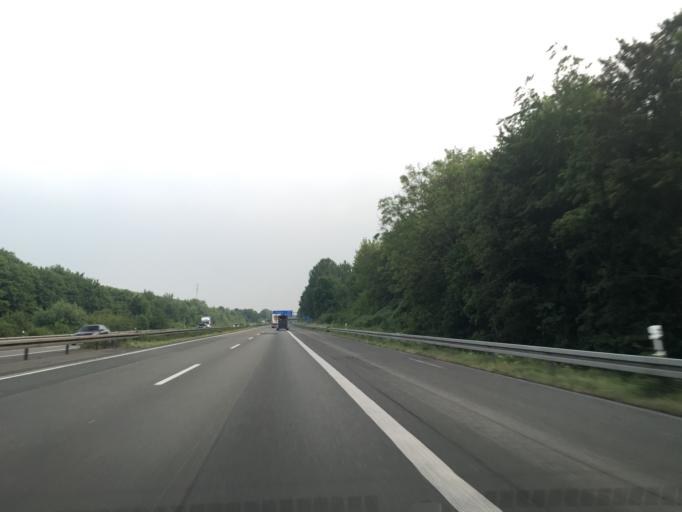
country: DE
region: North Rhine-Westphalia
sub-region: Regierungsbezirk Munster
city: Muenster
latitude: 52.0015
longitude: 7.5713
